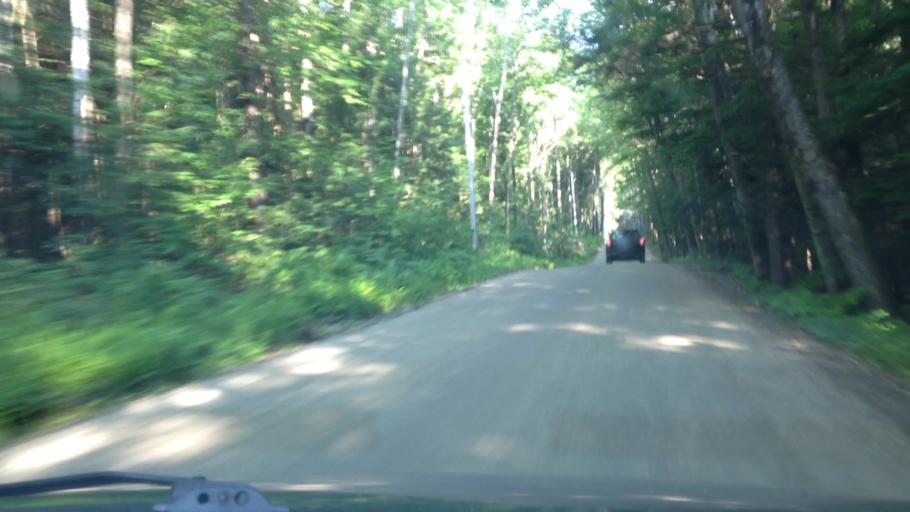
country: US
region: New Hampshire
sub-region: Cheshire County
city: Marlborough
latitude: 42.8955
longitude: -72.1911
